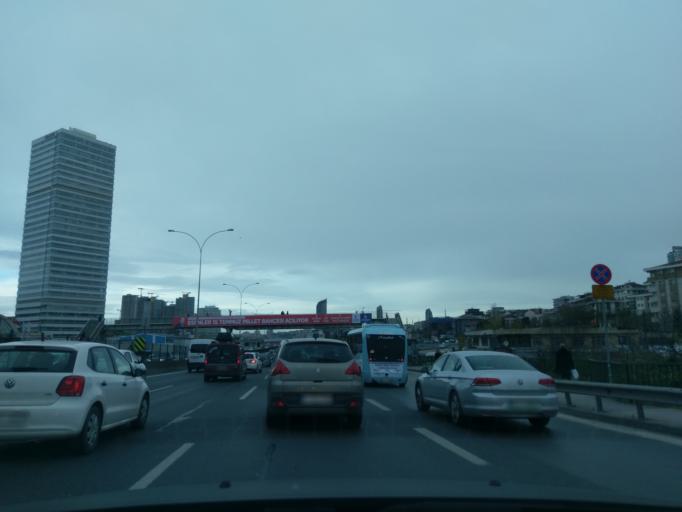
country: TR
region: Istanbul
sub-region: Atasehir
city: Atasehir
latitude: 40.9906
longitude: 29.0787
